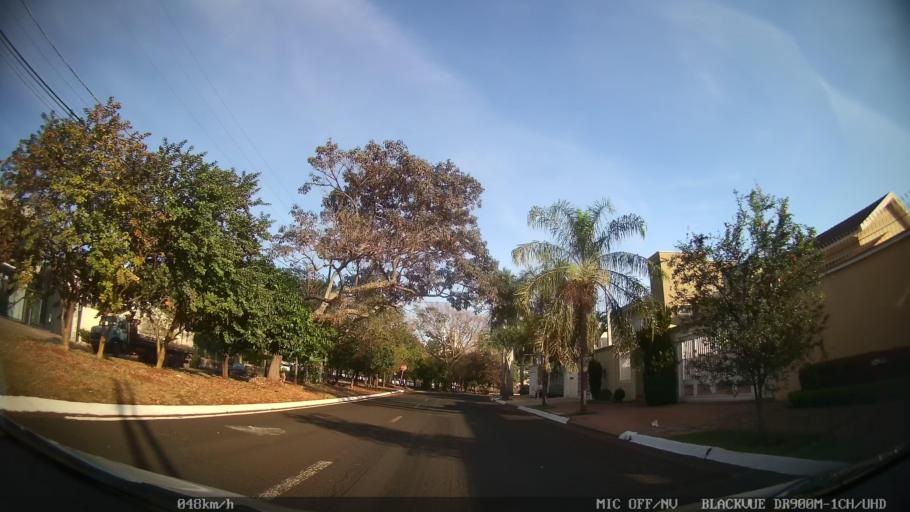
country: BR
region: Sao Paulo
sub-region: Ribeirao Preto
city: Ribeirao Preto
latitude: -21.2110
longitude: -47.7873
